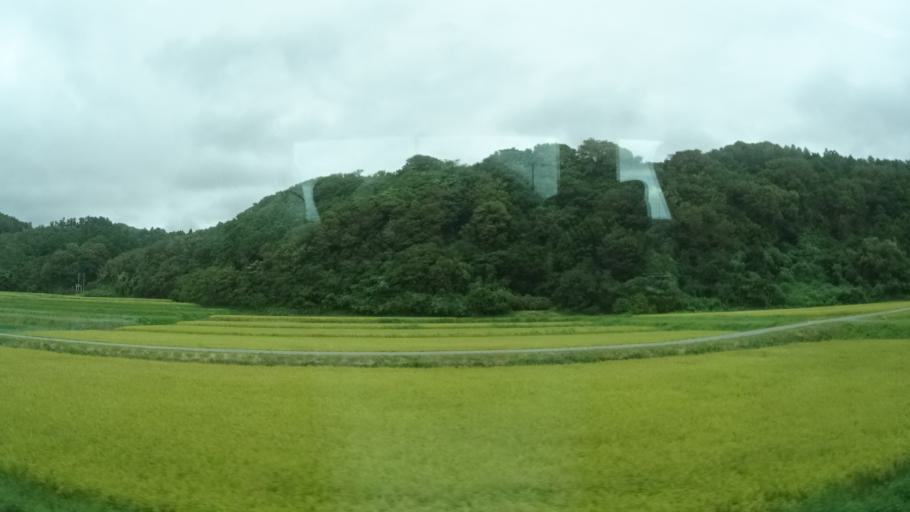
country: JP
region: Niigata
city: Murakami
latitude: 38.2787
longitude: 139.4509
